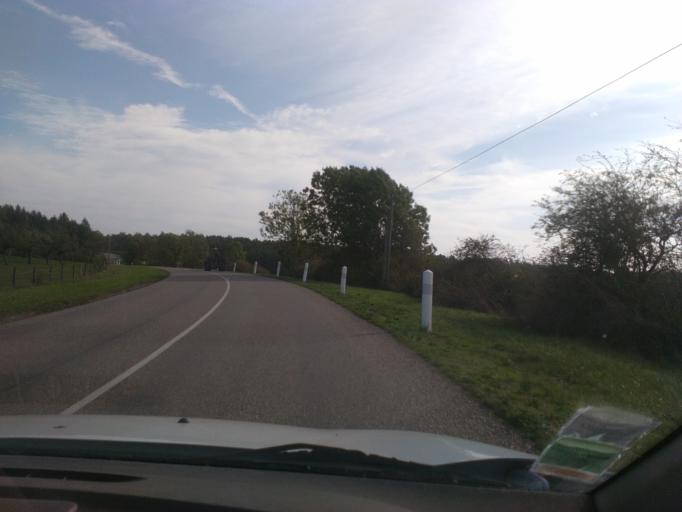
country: FR
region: Lorraine
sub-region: Departement des Vosges
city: Chatel-sur-Moselle
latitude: 48.3401
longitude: 6.4650
